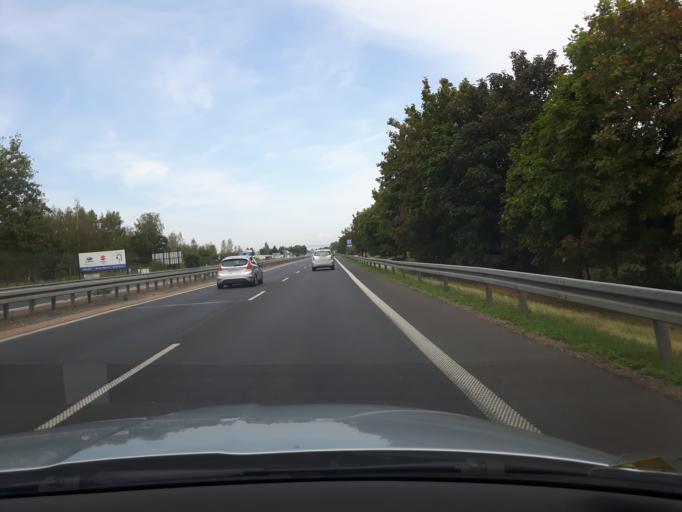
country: PL
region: Masovian Voivodeship
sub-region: Powiat warszawski zachodni
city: Kielpin
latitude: 52.3422
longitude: 20.8660
